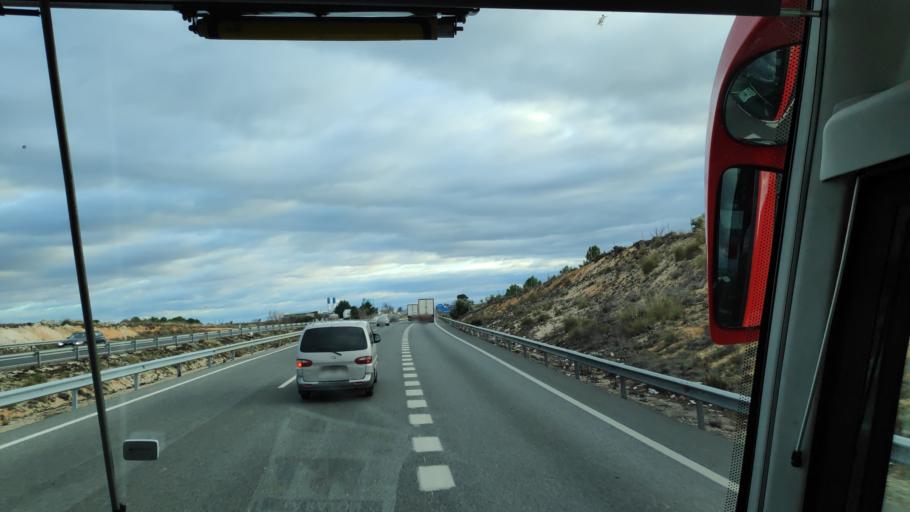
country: ES
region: Madrid
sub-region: Provincia de Madrid
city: Villarejo de Salvanes
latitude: 40.1888
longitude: -3.2989
